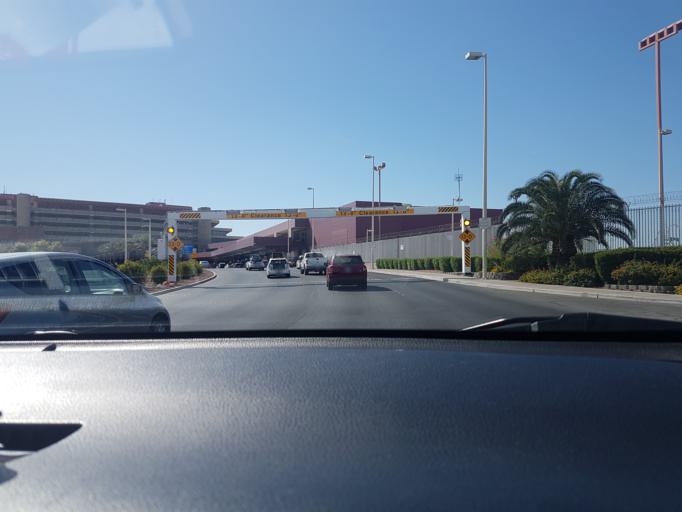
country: US
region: Nevada
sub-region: Clark County
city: Paradise
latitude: 36.0880
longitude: -115.1509
